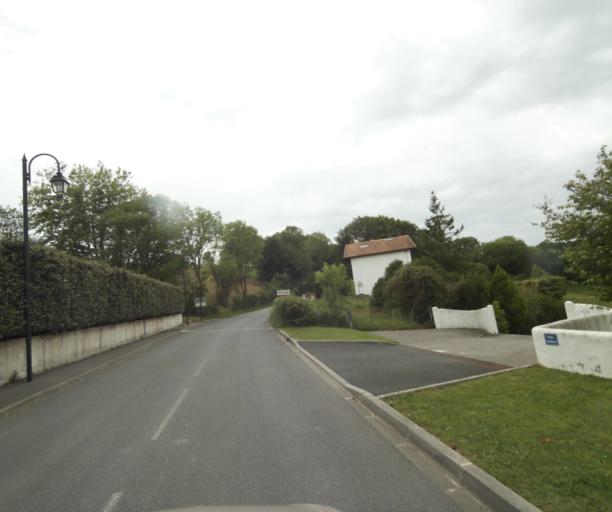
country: FR
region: Aquitaine
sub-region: Departement des Pyrenees-Atlantiques
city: Mouguerre
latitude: 43.4617
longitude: -1.4084
